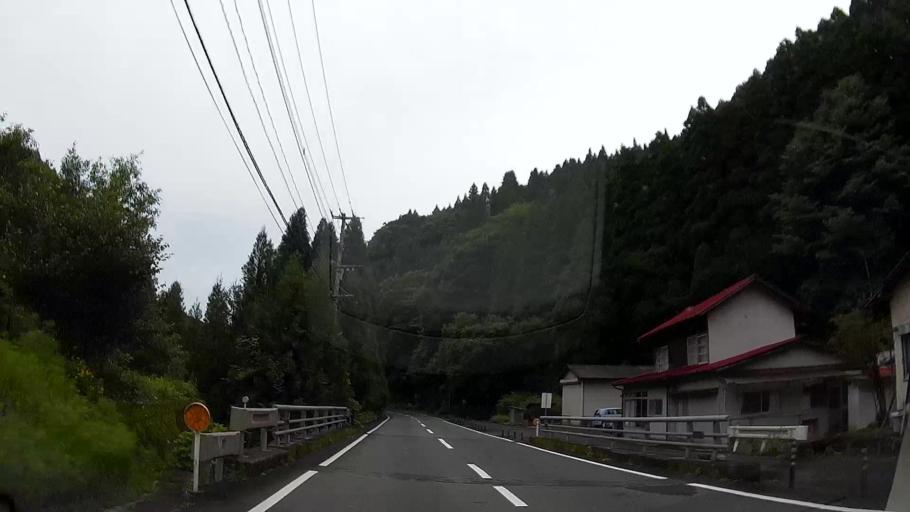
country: JP
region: Kumamoto
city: Kikuchi
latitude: 33.1094
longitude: 130.9615
